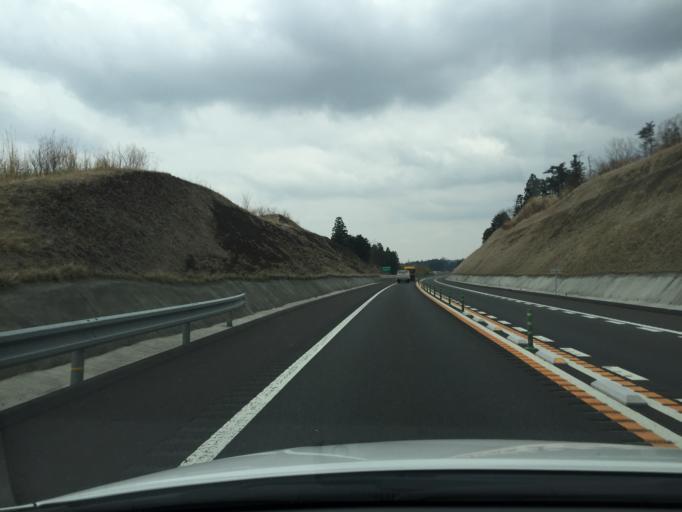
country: JP
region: Miyagi
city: Marumori
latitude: 37.8109
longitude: 140.8818
